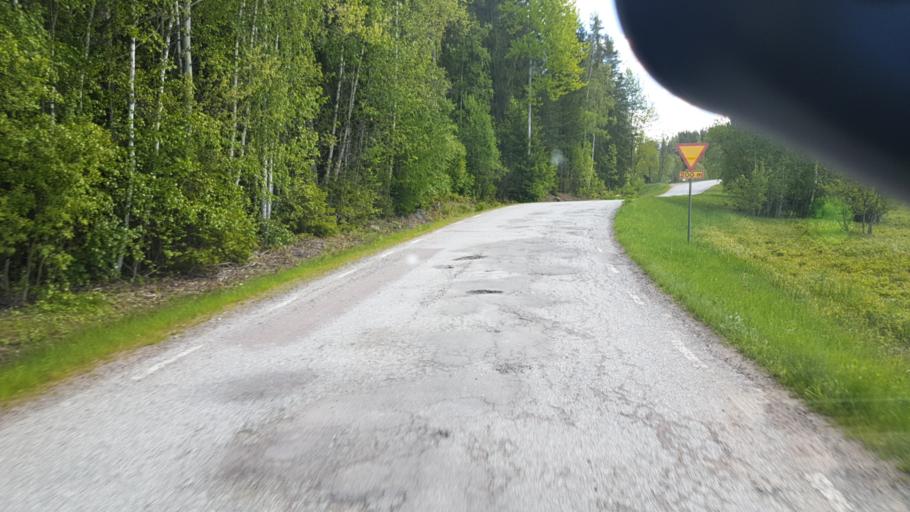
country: SE
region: Vaermland
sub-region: Sunne Kommun
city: Sunne
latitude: 59.6684
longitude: 12.9089
